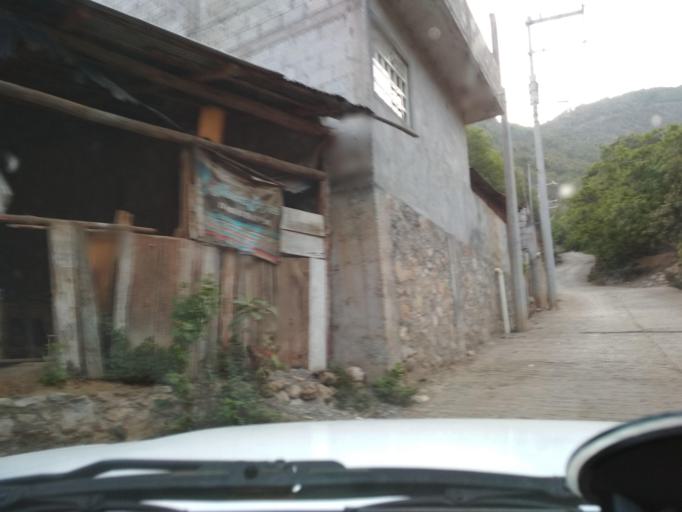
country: MX
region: Veracruz
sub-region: Nogales
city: Taza de Agua Ojo Zarco
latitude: 18.7714
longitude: -97.1932
